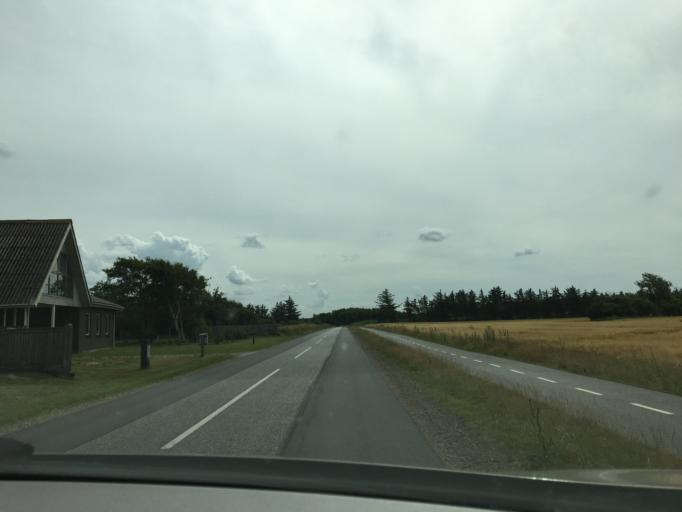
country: DK
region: Central Jutland
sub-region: Ringkobing-Skjern Kommune
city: Skjern
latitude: 55.9764
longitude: 8.3543
